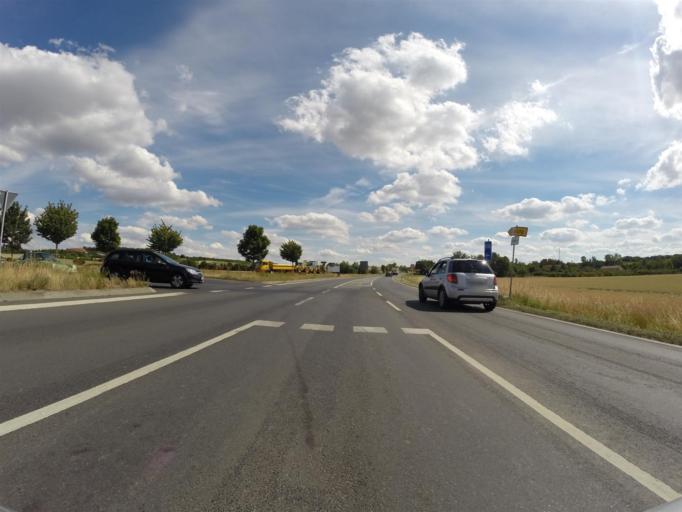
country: DE
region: Bavaria
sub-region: Regierungsbezirk Unterfranken
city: Volkach
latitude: 49.8558
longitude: 10.2295
